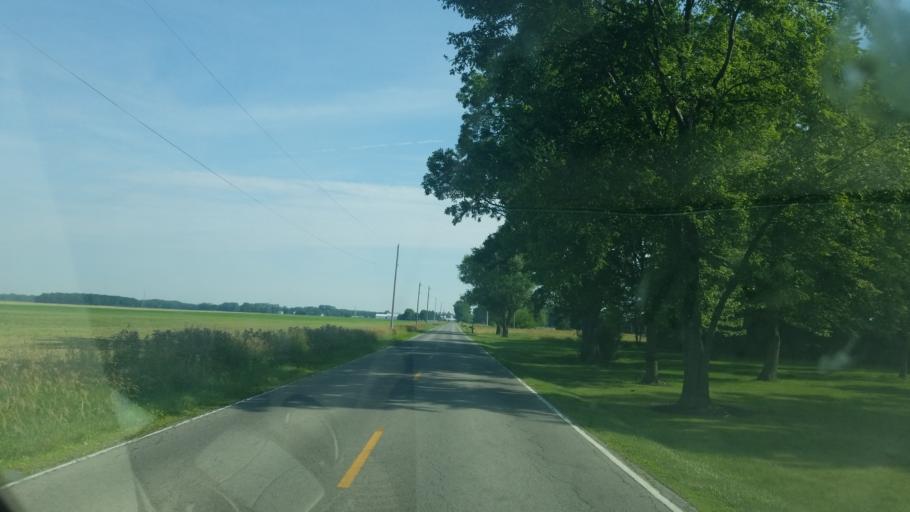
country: US
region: Ohio
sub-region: Hancock County
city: Findlay
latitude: 41.0131
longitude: -83.5881
